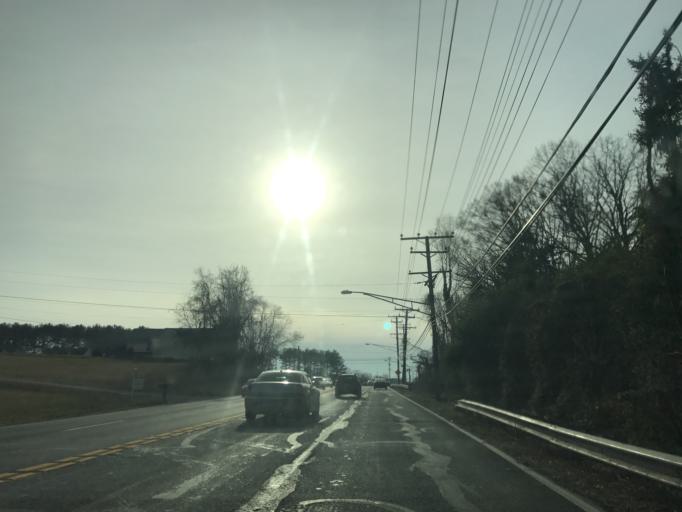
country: US
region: Maryland
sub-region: Baltimore County
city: Perry Hall
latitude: 39.4219
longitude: -76.4530
